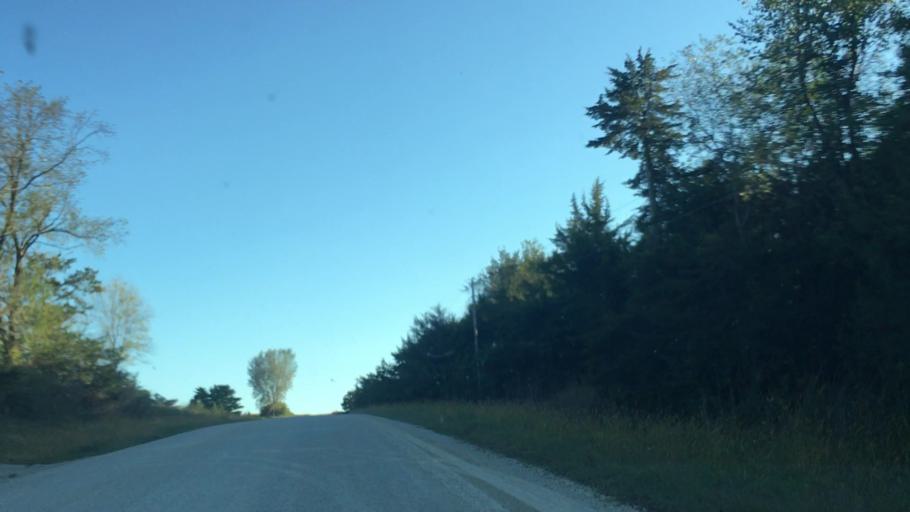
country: US
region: Minnesota
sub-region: Fillmore County
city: Preston
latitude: 43.7773
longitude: -92.0294
